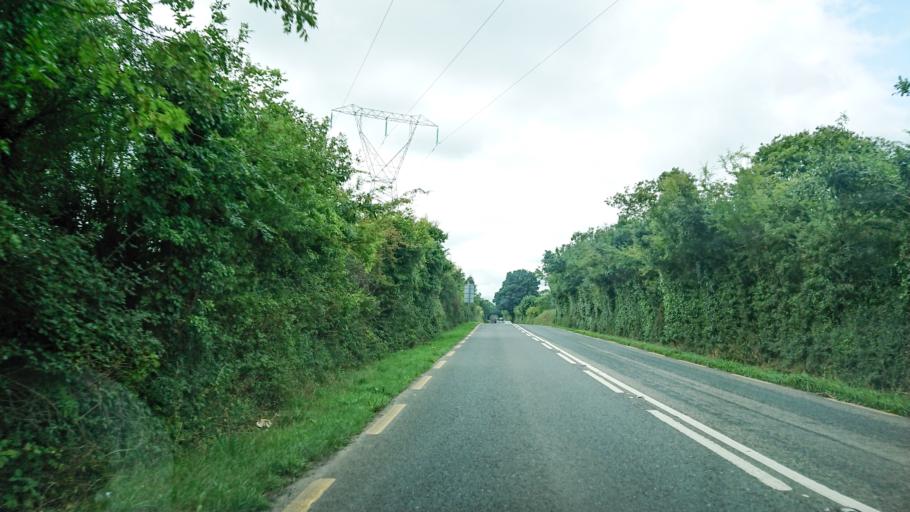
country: IE
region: Munster
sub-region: Waterford
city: Dungarvan
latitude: 52.1098
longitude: -7.6788
